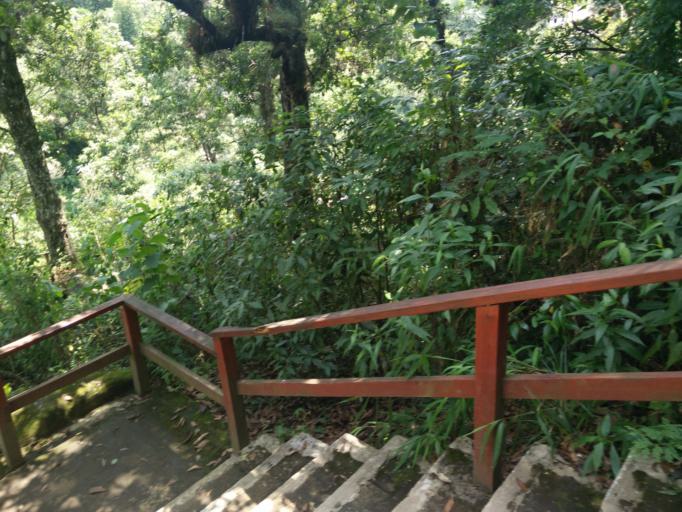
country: MX
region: Veracruz
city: Xico
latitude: 19.4013
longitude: -96.9950
